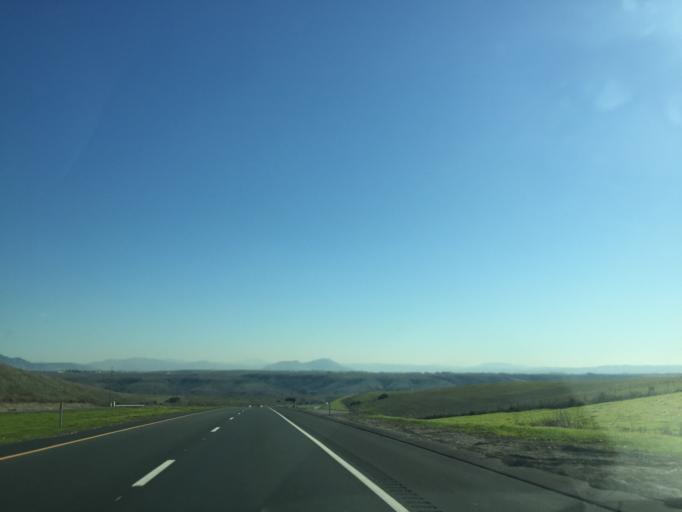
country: US
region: California
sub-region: San Diego County
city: Bonita
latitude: 32.6088
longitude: -116.9677
